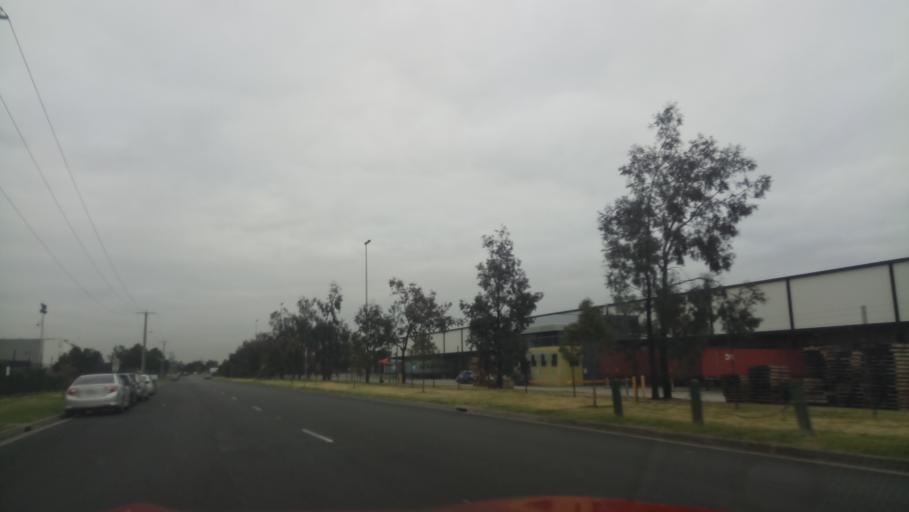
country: AU
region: Victoria
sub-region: Hobsons Bay
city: Altona
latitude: -37.8470
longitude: 144.8153
